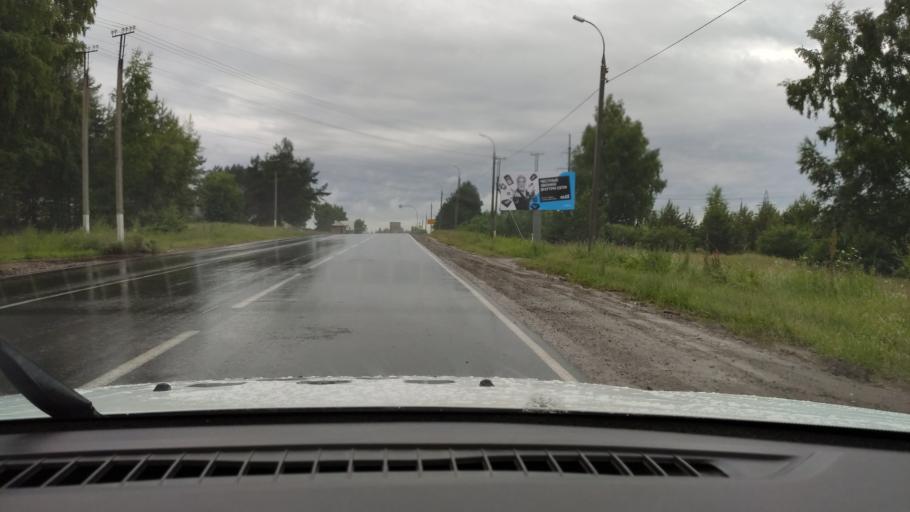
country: RU
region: Udmurtiya
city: Votkinsk
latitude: 57.0328
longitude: 53.9333
